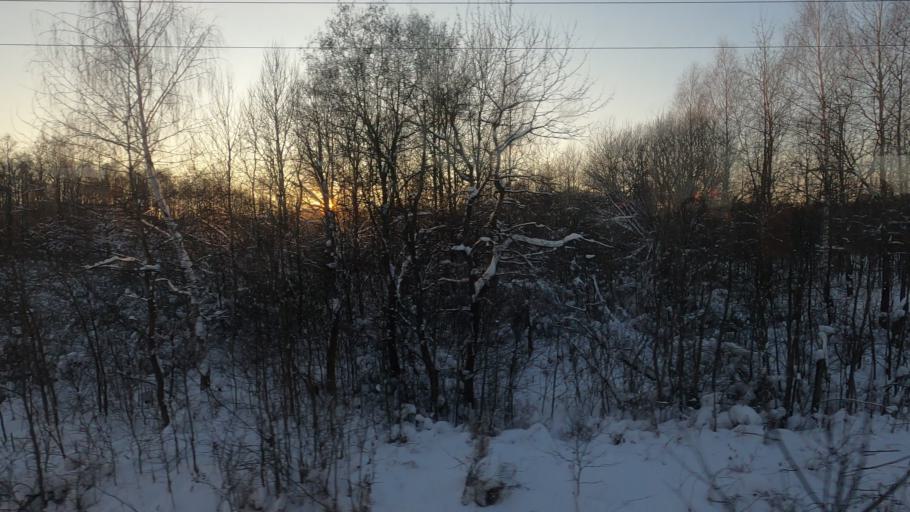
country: RU
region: Moskovskaya
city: Dmitrov
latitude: 56.3880
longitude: 37.5102
